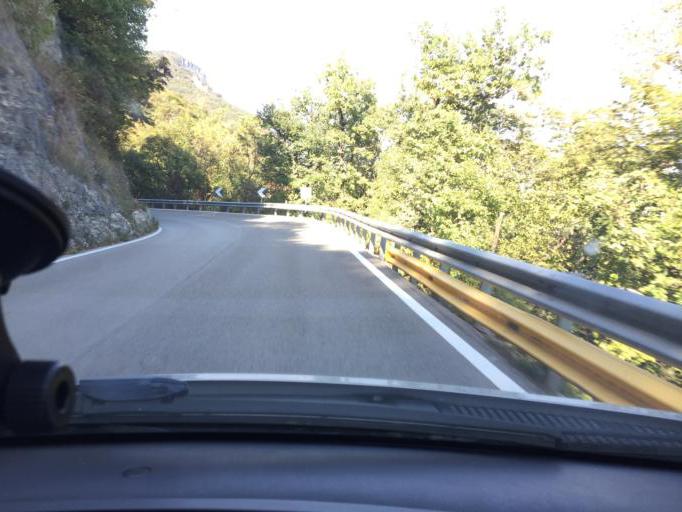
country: IT
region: Trentino-Alto Adige
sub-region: Provincia di Trento
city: Trento
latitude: 46.0708
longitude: 11.0951
